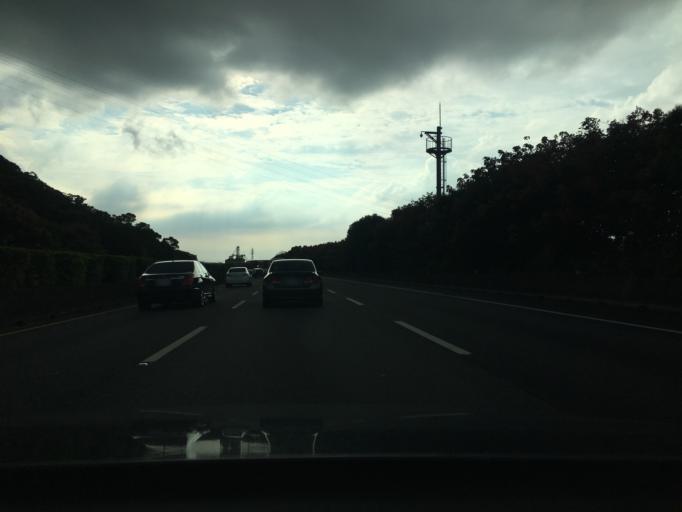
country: TW
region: Taiwan
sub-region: Hsinchu
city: Zhubei
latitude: 24.8843
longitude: 121.0788
